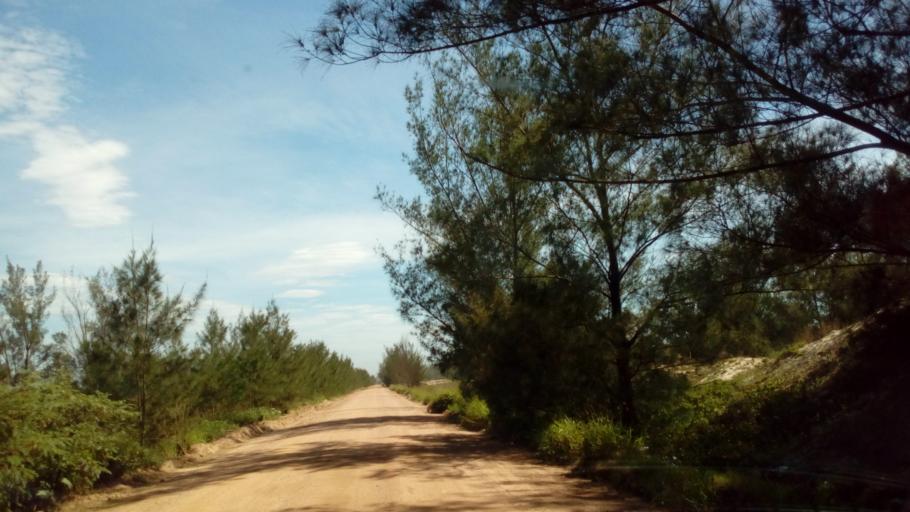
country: BR
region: Santa Catarina
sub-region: Laguna
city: Laguna
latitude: -28.4547
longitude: -48.7653
